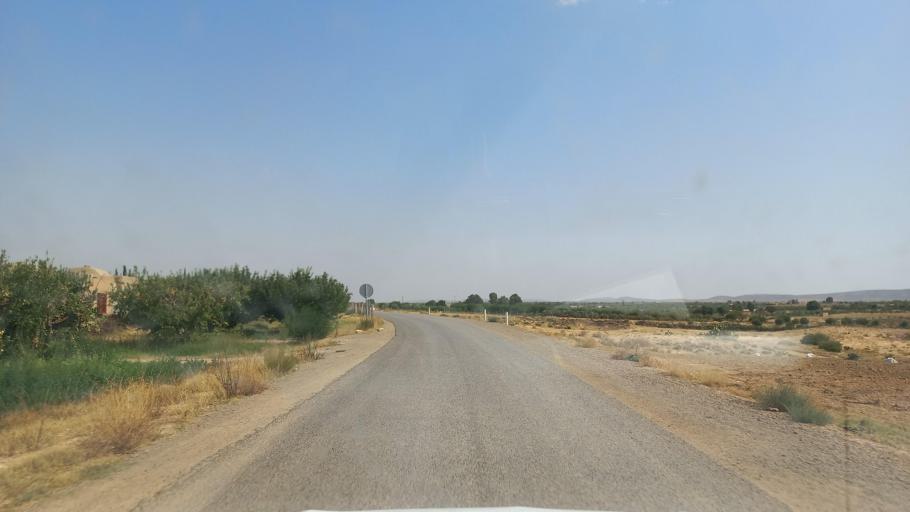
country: TN
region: Al Qasrayn
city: Kasserine
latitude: 35.2409
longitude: 9.0294
